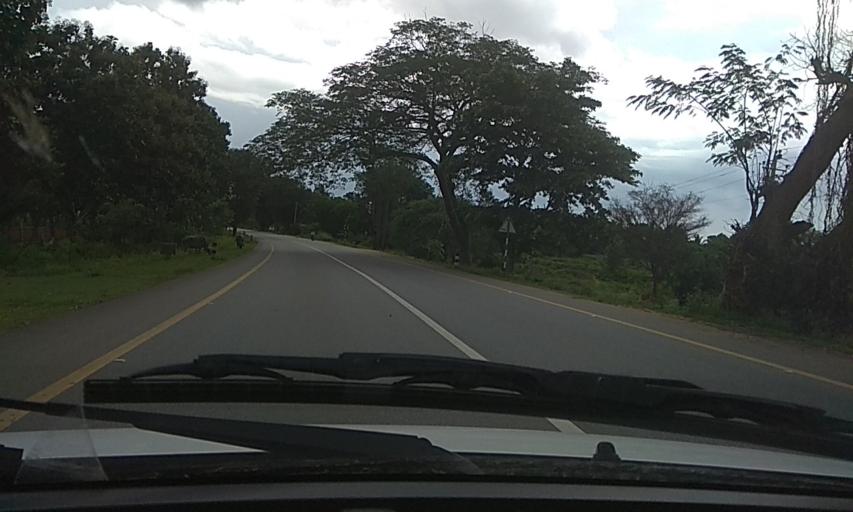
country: IN
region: Karnataka
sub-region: Tumkur
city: Kunigal
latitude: 13.1325
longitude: 77.0296
